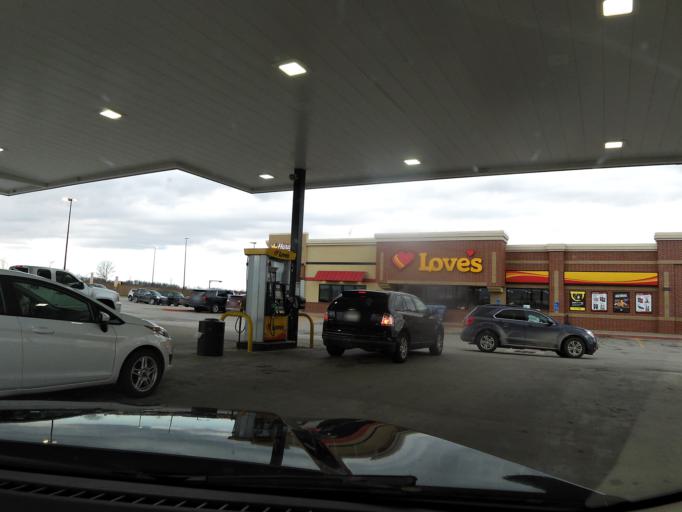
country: US
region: Missouri
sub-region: Ralls County
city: New London
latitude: 39.5739
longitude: -91.4033
